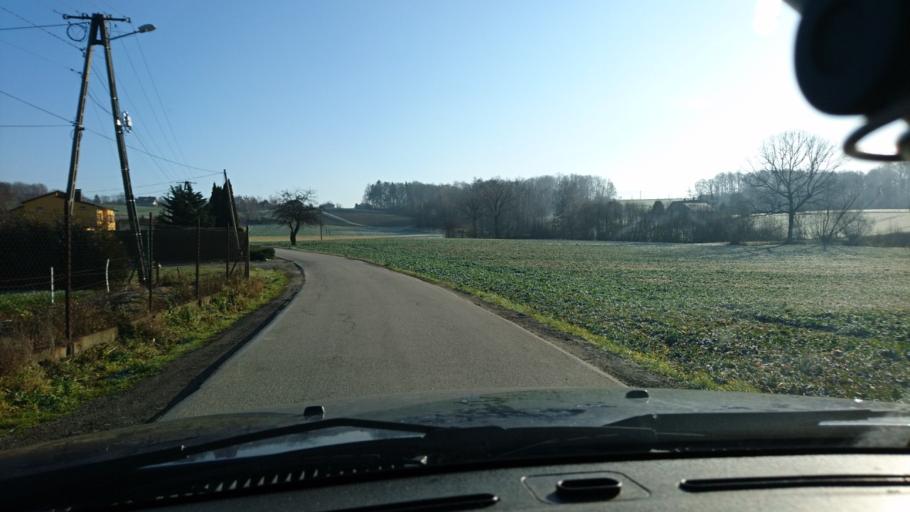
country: PL
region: Silesian Voivodeship
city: Janowice
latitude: 49.8944
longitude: 19.1071
